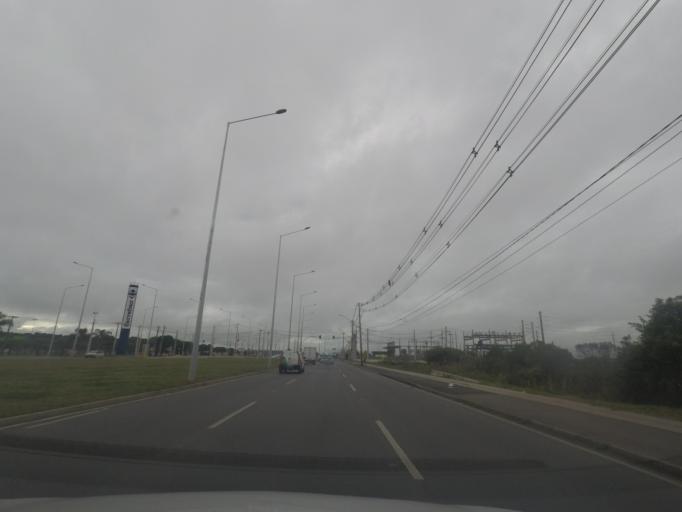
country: BR
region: Parana
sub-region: Pinhais
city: Pinhais
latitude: -25.4367
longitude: -49.1675
